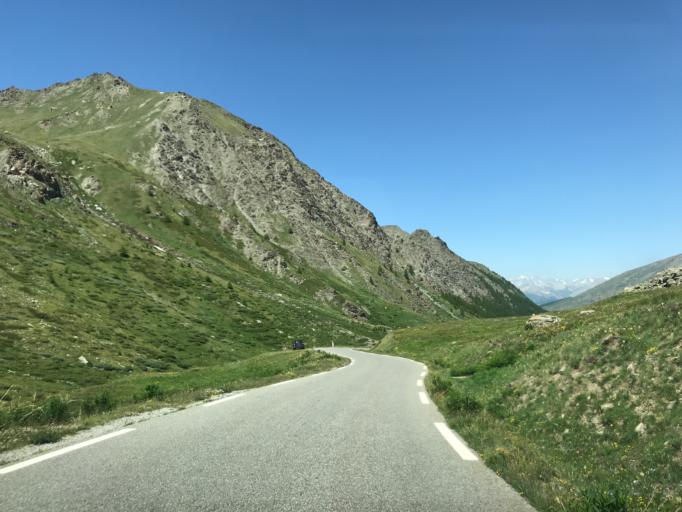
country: IT
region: Piedmont
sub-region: Provincia di Cuneo
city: Pontechianale
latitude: 44.6958
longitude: 6.9506
